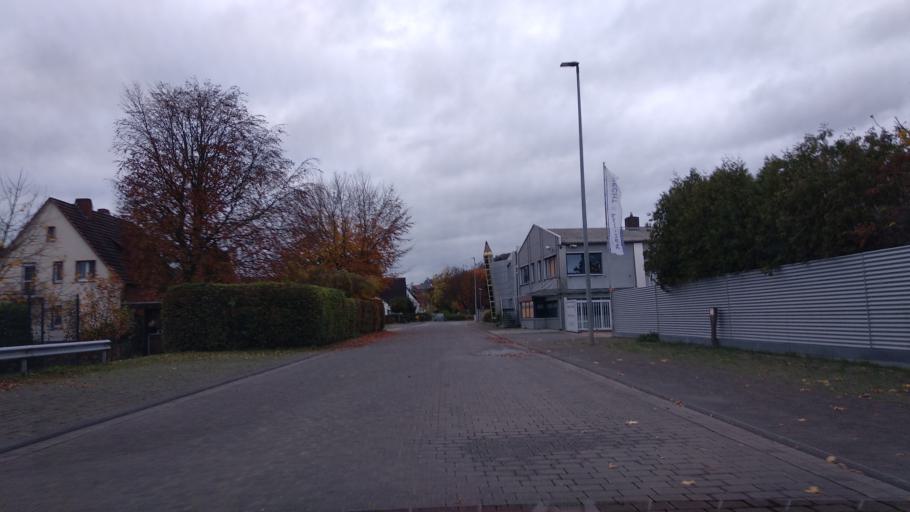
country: DE
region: North Rhine-Westphalia
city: Beverungen
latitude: 51.6717
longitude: 9.3809
